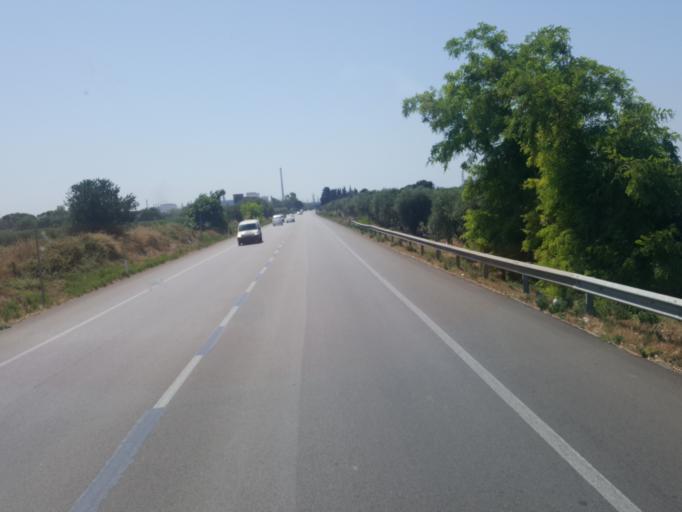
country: IT
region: Apulia
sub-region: Provincia di Taranto
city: Statte
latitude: 40.5231
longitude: 17.1762
